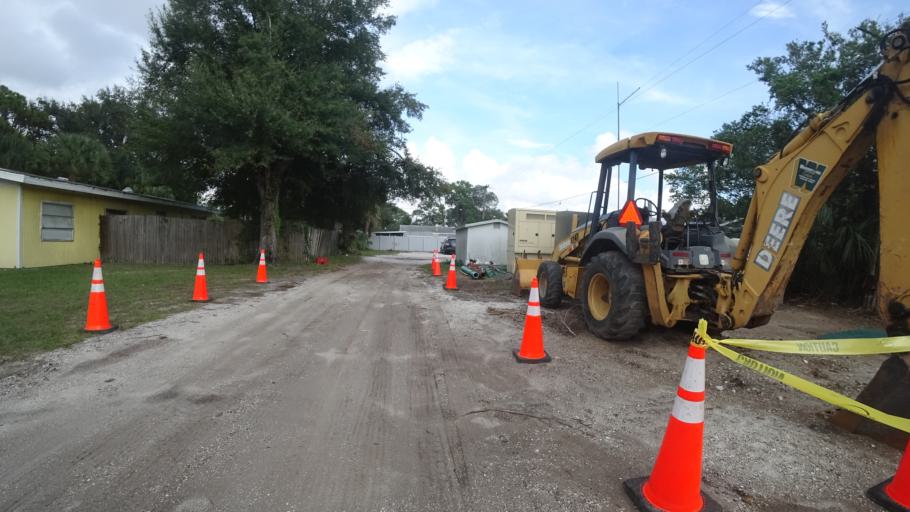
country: US
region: Florida
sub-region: Manatee County
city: South Bradenton
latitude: 27.4570
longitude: -82.5799
